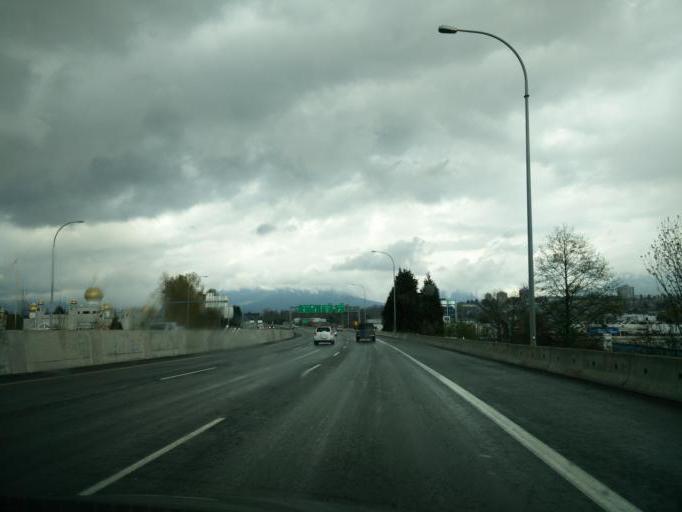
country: CA
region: British Columbia
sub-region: Fraser Valley Regional District
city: North Vancouver
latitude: 49.2654
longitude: -123.0259
